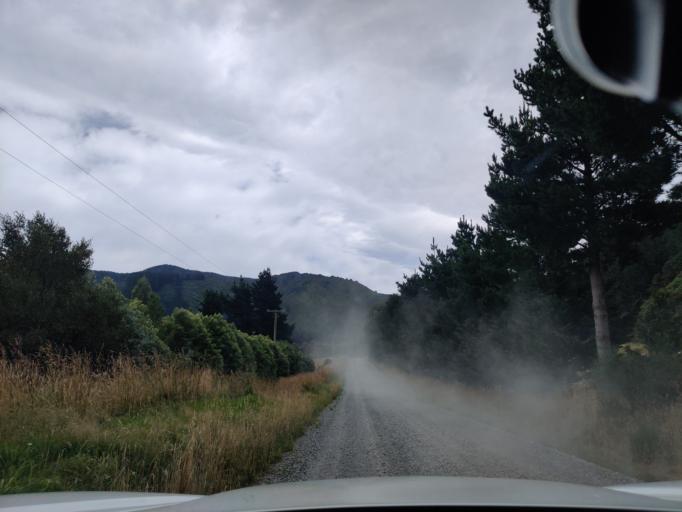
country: NZ
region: Wellington
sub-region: Masterton District
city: Masterton
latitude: -41.0384
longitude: 175.4023
